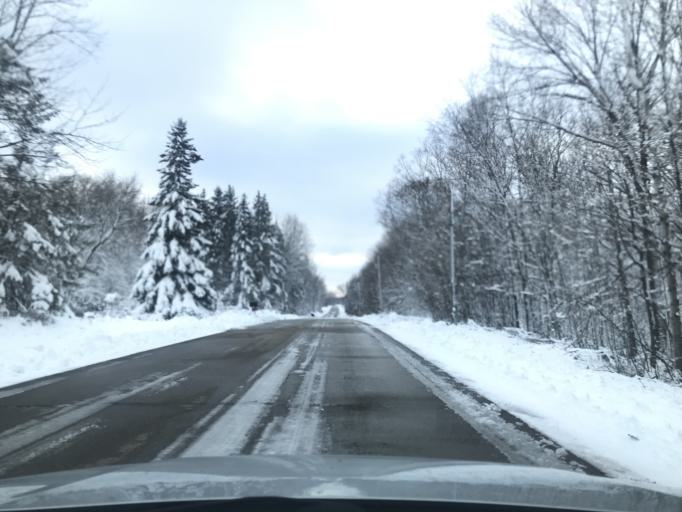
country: US
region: Wisconsin
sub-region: Oconto County
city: Oconto Falls
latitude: 44.9111
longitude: -88.0083
